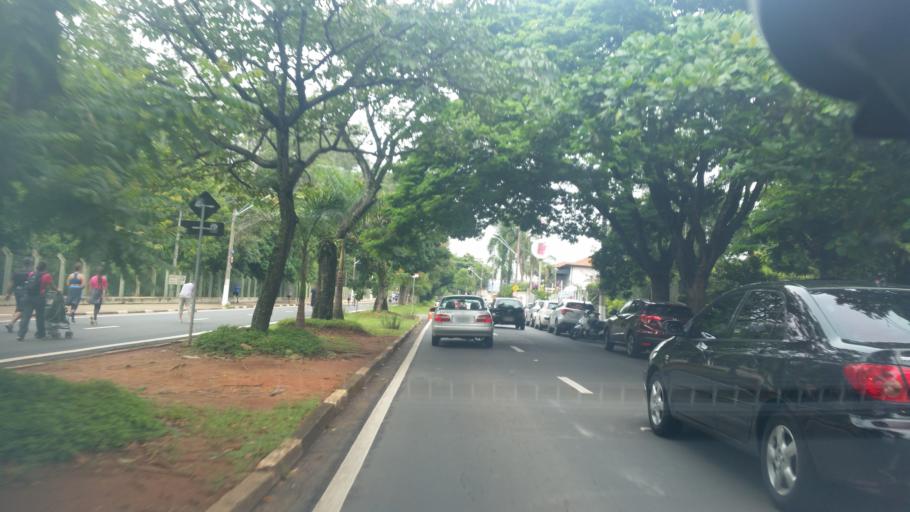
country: BR
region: Sao Paulo
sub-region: Campinas
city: Campinas
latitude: -22.8723
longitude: -47.0492
